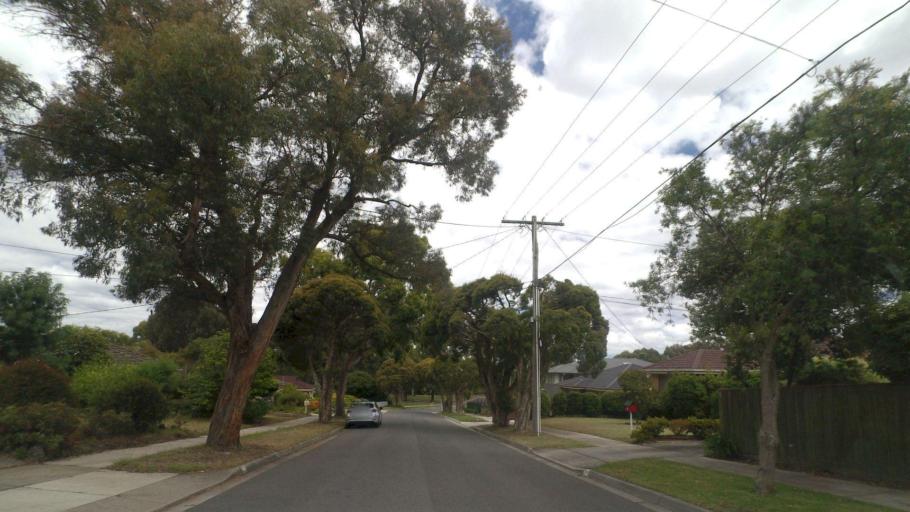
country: AU
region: Victoria
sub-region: Knox
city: Bayswater
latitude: -37.8635
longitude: 145.2448
